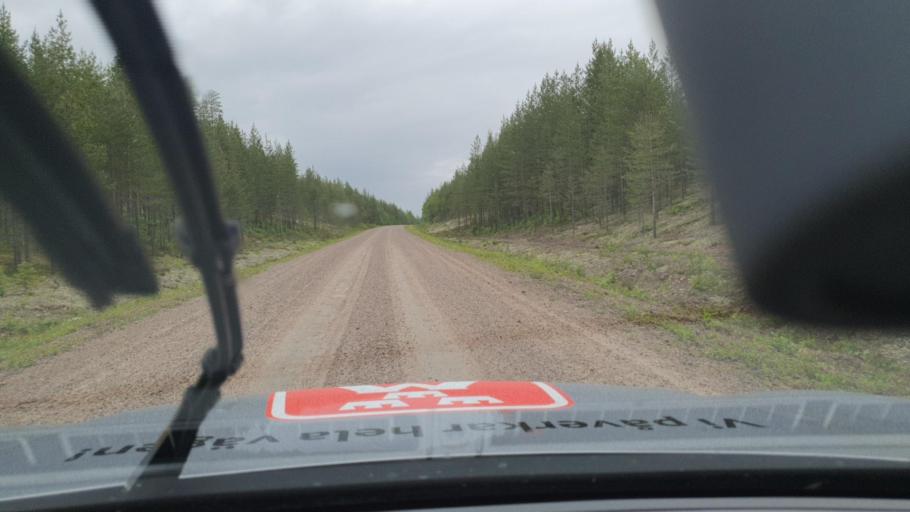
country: SE
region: Norrbotten
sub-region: Overkalix Kommun
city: OEverkalix
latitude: 66.5717
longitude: 22.7473
